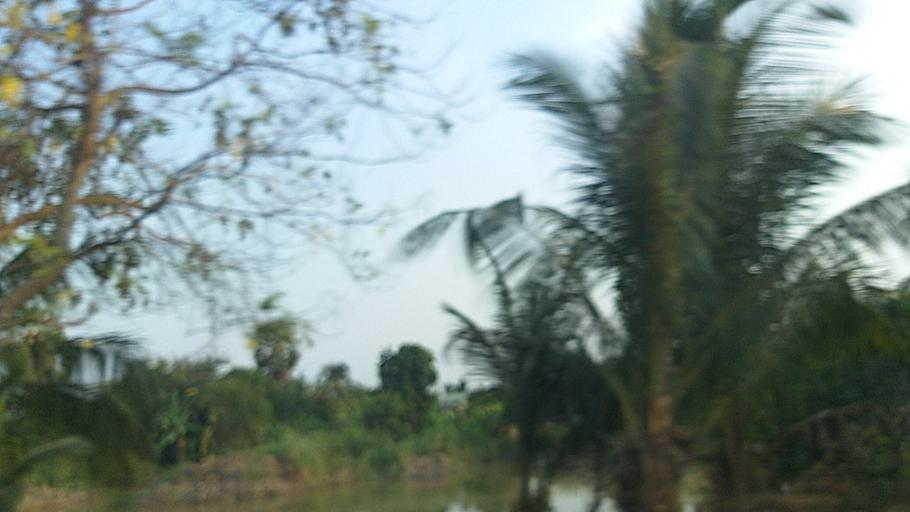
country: TH
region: Nakhon Nayok
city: Ongkharak
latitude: 14.1075
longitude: 100.9725
